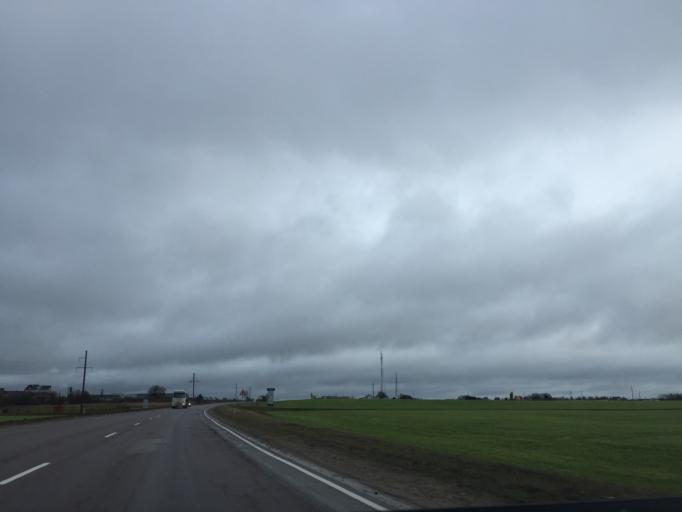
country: LV
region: Saldus Rajons
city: Saldus
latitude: 56.6792
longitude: 22.4533
